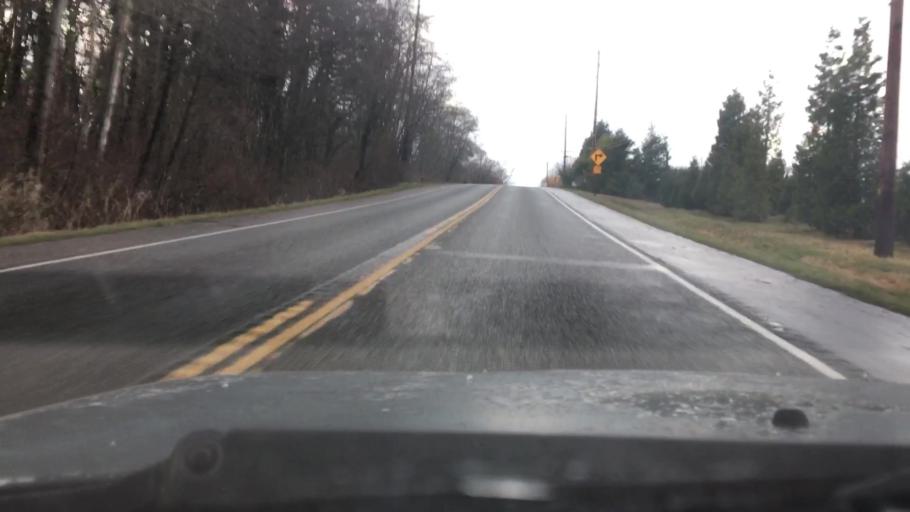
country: US
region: Washington
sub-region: Whatcom County
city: Ferndale
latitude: 48.8195
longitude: -122.6788
